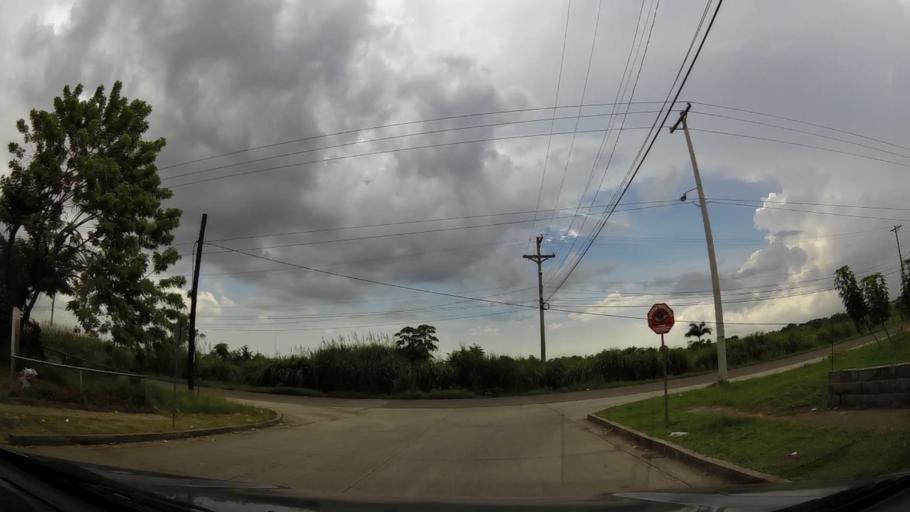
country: PA
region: Panama
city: Cabra Numero Uno
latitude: 9.1096
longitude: -79.3125
